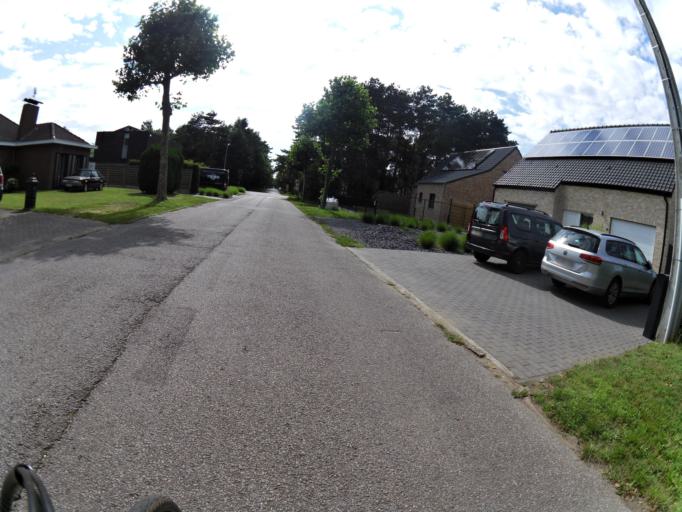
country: BE
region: Flanders
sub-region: Provincie Antwerpen
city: Balen
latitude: 51.1924
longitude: 5.2137
